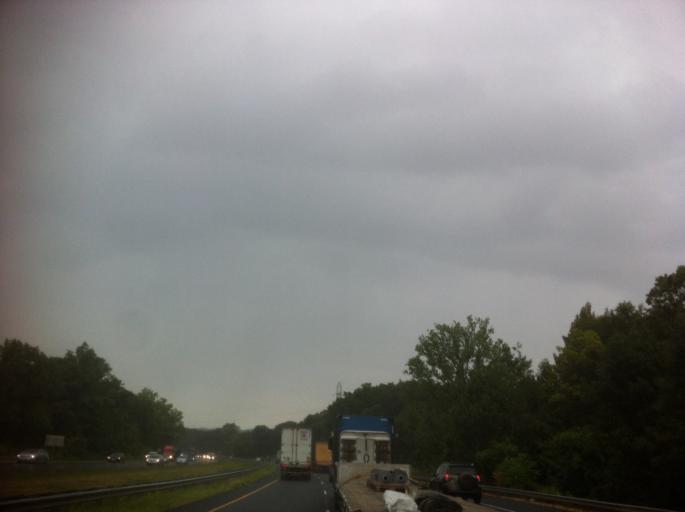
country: US
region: New Jersey
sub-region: Morris County
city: Rockaway
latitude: 40.9114
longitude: -74.5138
